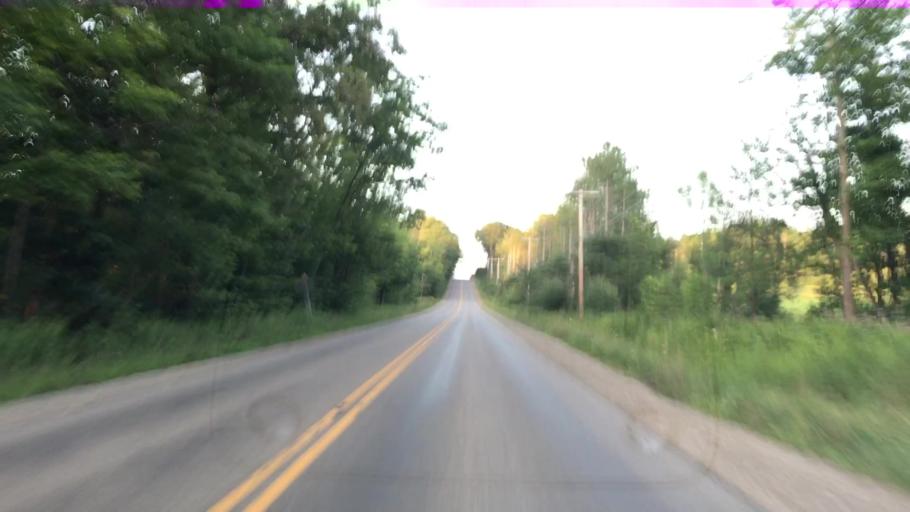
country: US
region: New York
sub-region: Chautauqua County
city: Mayville
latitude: 42.2722
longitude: -79.4612
